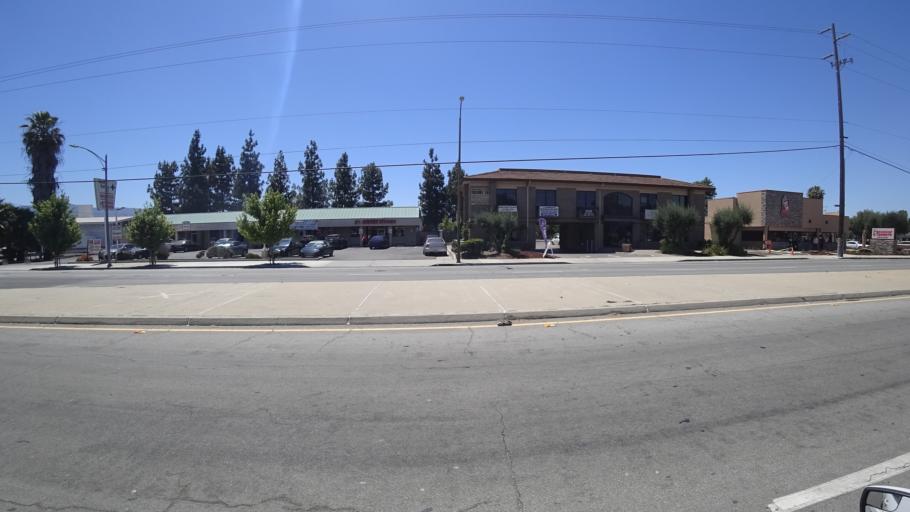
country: US
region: California
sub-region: Santa Clara County
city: Seven Trees
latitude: 37.2522
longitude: -121.8308
